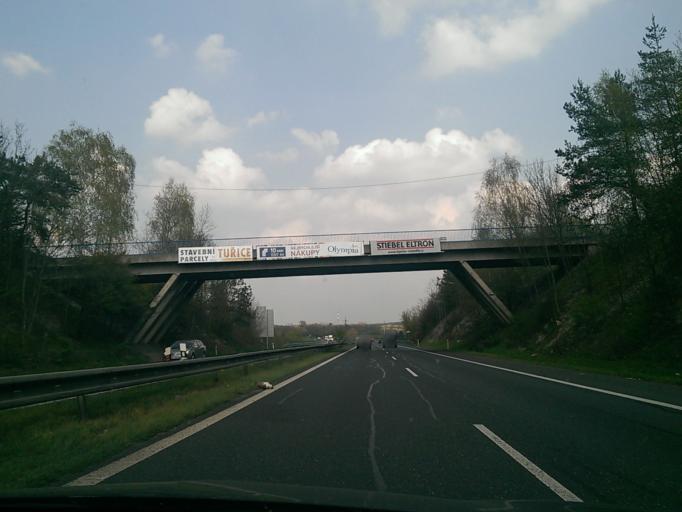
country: CZ
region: Central Bohemia
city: Benatky nad Jizerou
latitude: 50.2536
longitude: 14.7648
